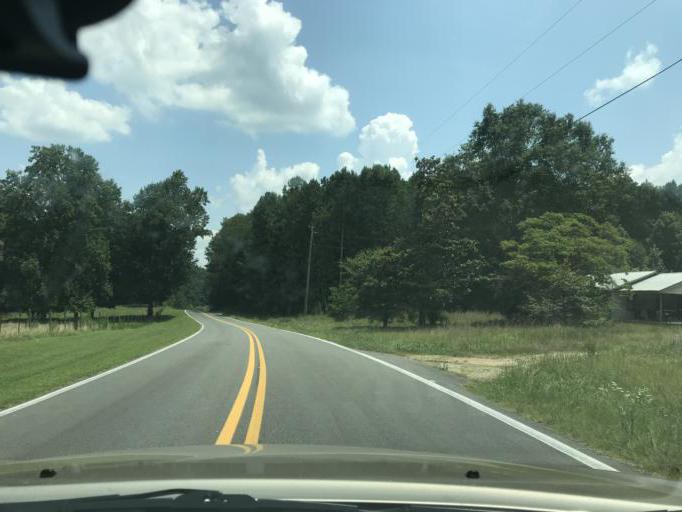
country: US
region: Georgia
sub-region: Forsyth County
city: Cumming
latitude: 34.2670
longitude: -84.2318
